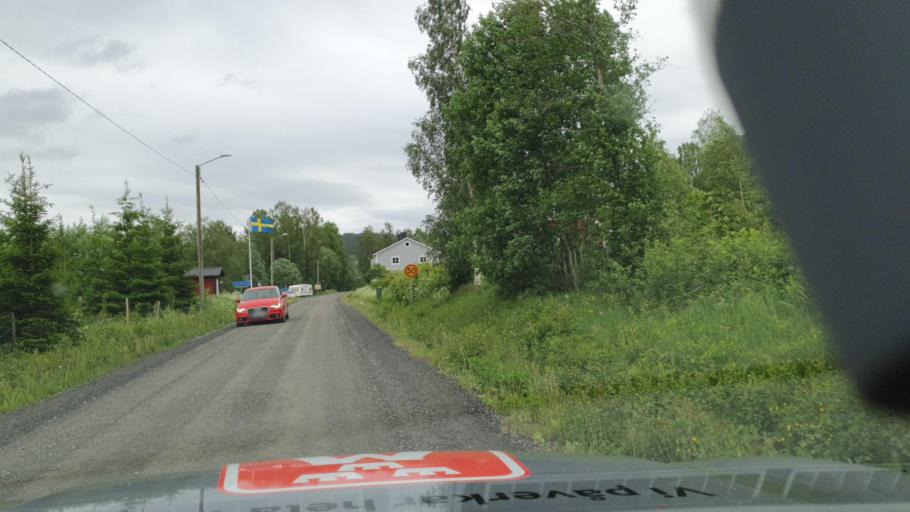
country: SE
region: Vaesternorrland
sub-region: Kramfors Kommun
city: Nordingra
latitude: 62.9941
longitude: 18.2716
